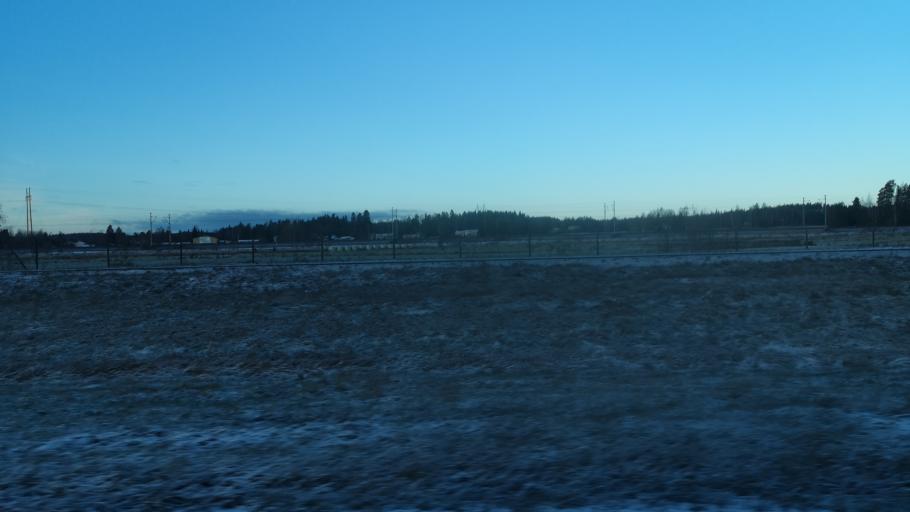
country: FI
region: Uusimaa
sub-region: Helsinki
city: Maentsaelae
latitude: 60.6159
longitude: 25.2718
